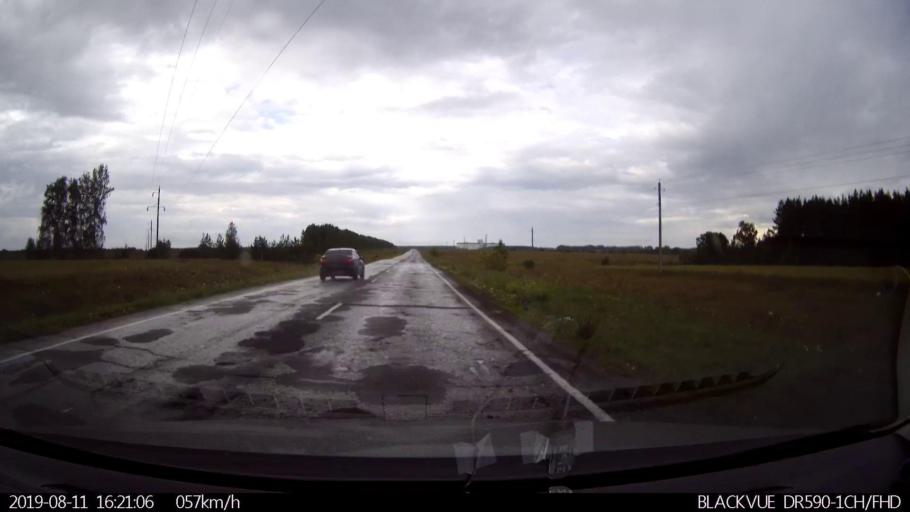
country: RU
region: Ulyanovsk
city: Mayna
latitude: 54.0772
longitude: 47.5996
